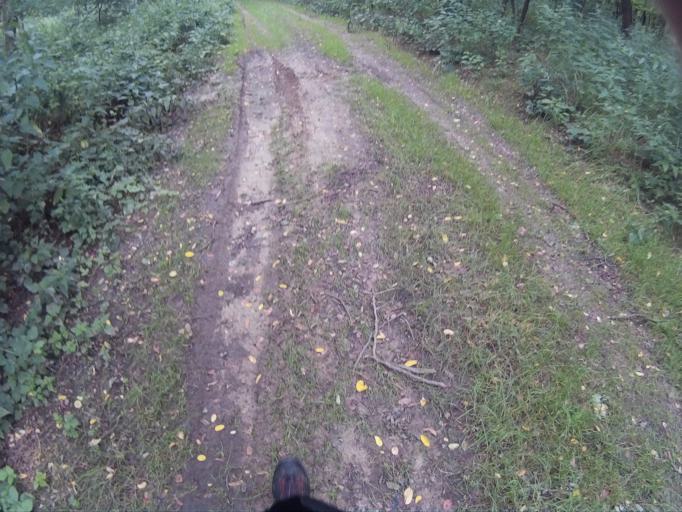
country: HU
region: Veszprem
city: Papa
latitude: 47.2788
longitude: 17.5687
